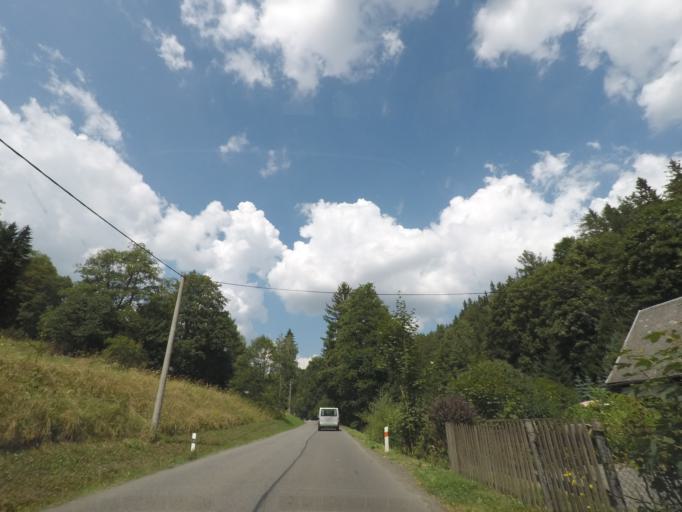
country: CZ
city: Radvanice
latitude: 50.6208
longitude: 16.1032
